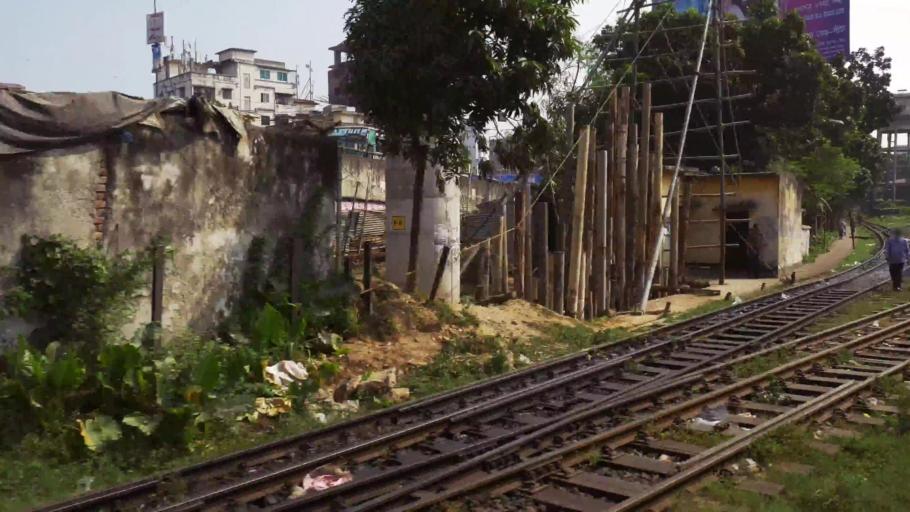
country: BD
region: Dhaka
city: Paltan
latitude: 23.7481
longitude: 90.4230
